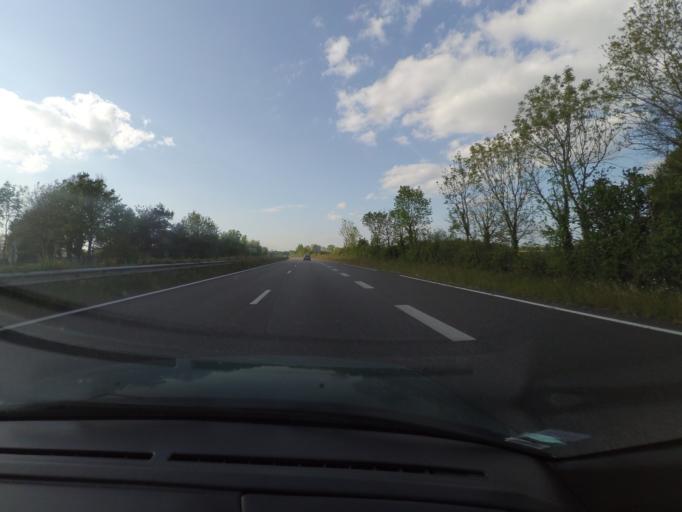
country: FR
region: Pays de la Loire
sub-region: Departement de la Vendee
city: Belleville-sur-Vie
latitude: 46.7839
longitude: -1.4206
